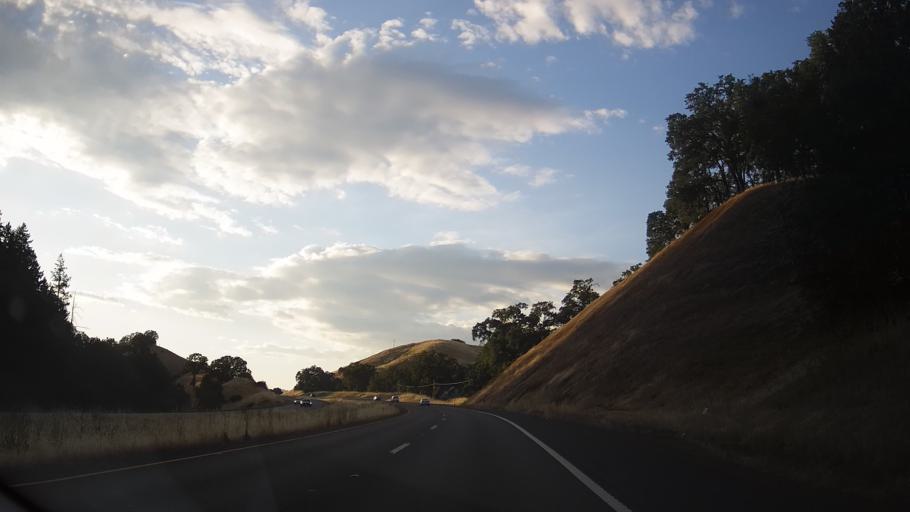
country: US
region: California
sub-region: Mendocino County
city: Talmage
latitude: 39.0690
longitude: -123.1686
